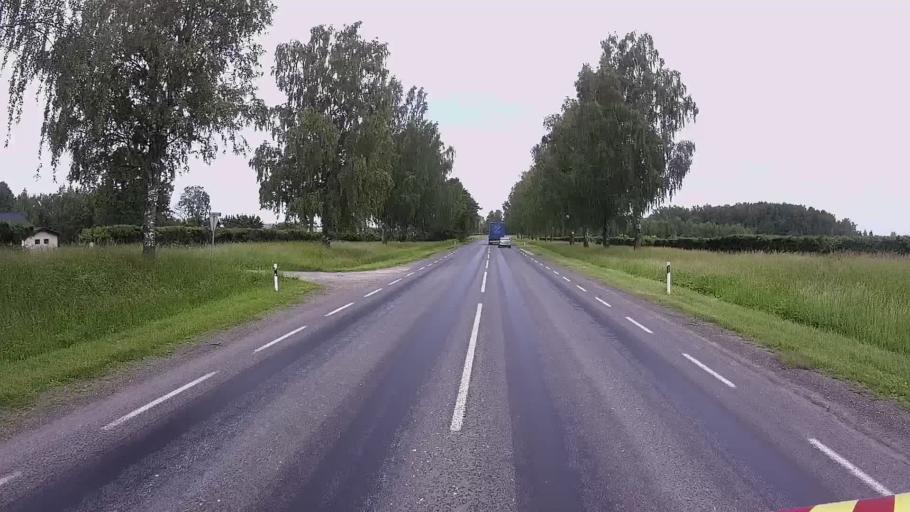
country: EE
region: Viljandimaa
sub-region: Viljandi linn
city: Viljandi
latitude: 58.3086
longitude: 25.5732
